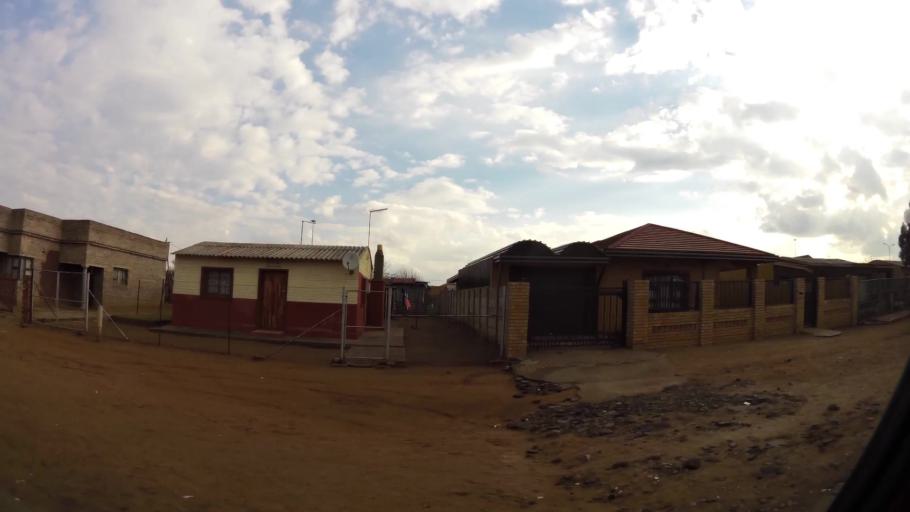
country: ZA
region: Gauteng
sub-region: Sedibeng District Municipality
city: Vanderbijlpark
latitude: -26.6841
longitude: 27.8783
